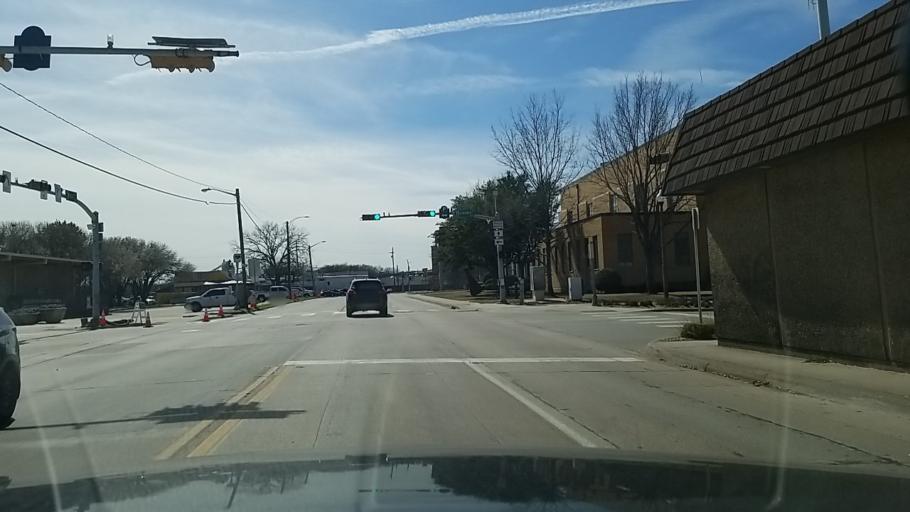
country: US
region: Texas
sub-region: Denton County
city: Denton
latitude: 33.2147
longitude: -97.1282
